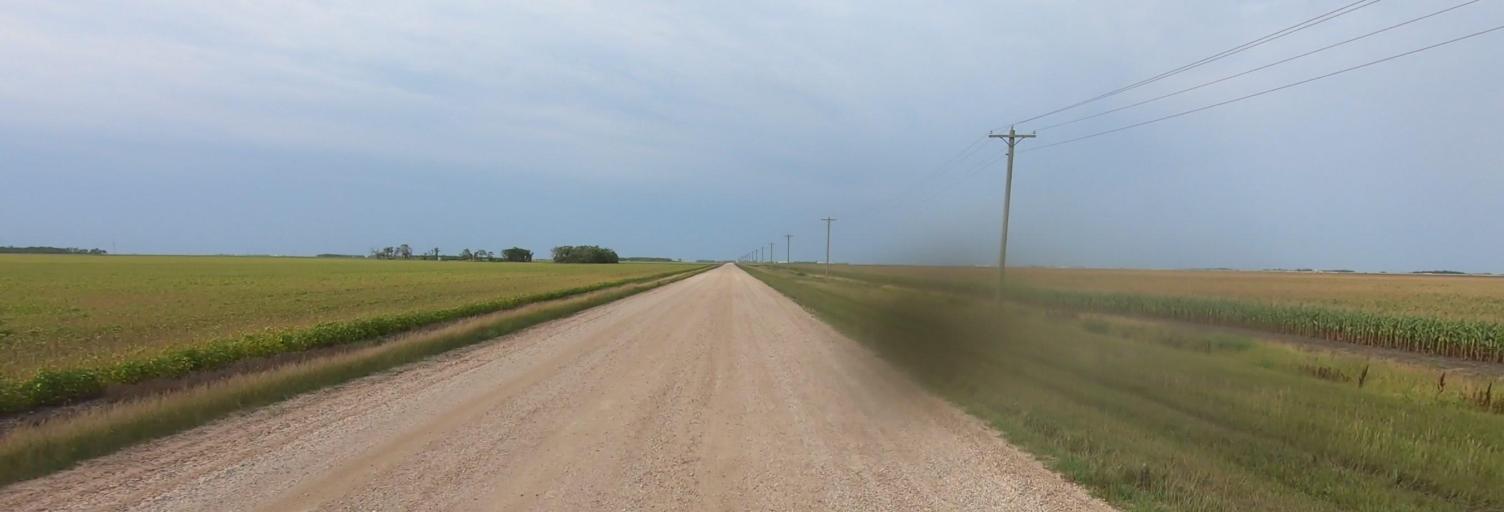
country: CA
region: Manitoba
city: Morris
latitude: 49.5766
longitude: -97.2800
